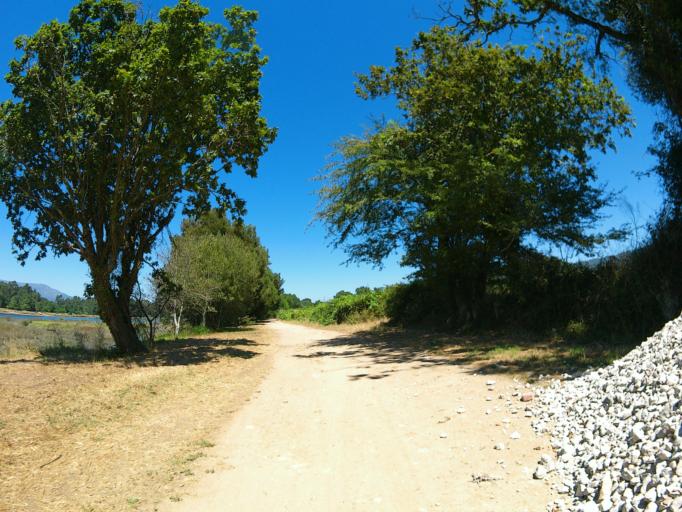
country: PT
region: Viana do Castelo
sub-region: Viana do Castelo
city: Darque
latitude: 41.7012
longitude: -8.7305
